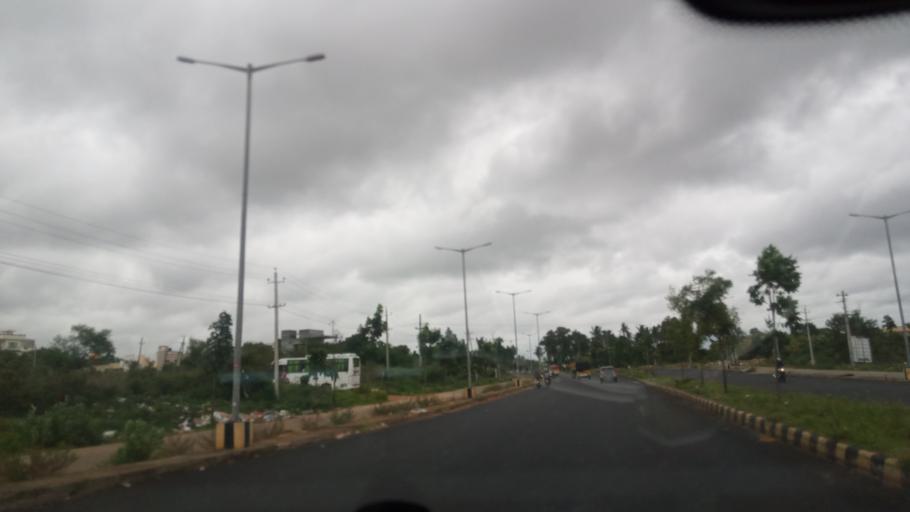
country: IN
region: Karnataka
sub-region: Mysore
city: Mysore
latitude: 12.2982
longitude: 76.6030
